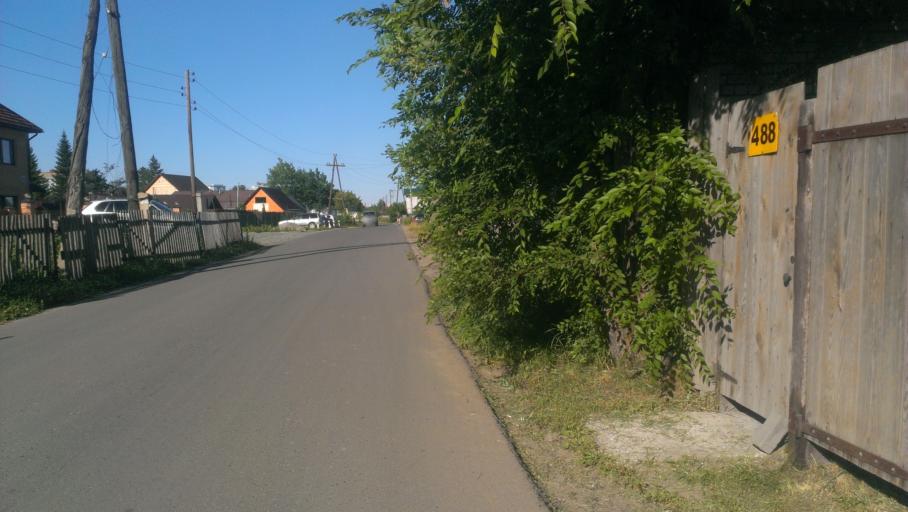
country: RU
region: Altai Krai
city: Novosilikatnyy
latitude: 53.3205
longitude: 83.6784
